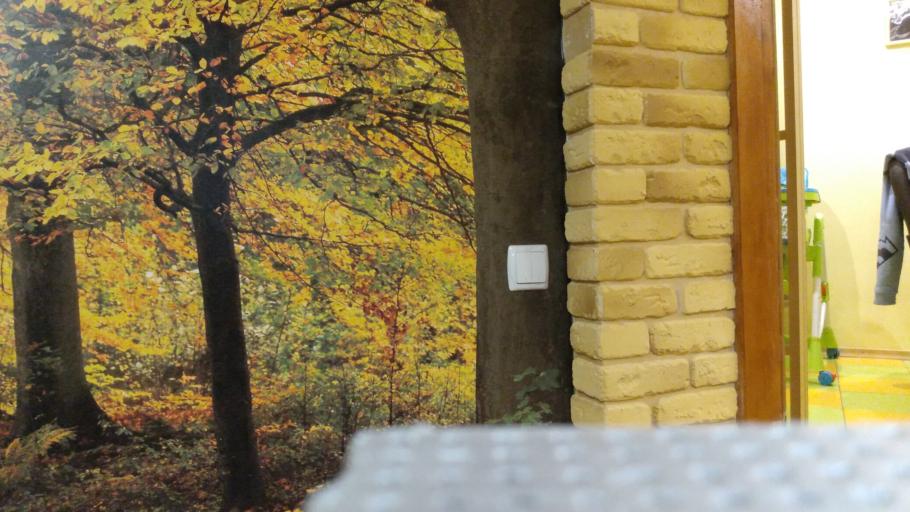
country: RU
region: Vologda
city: Babayevo
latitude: 59.3645
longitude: 35.9997
